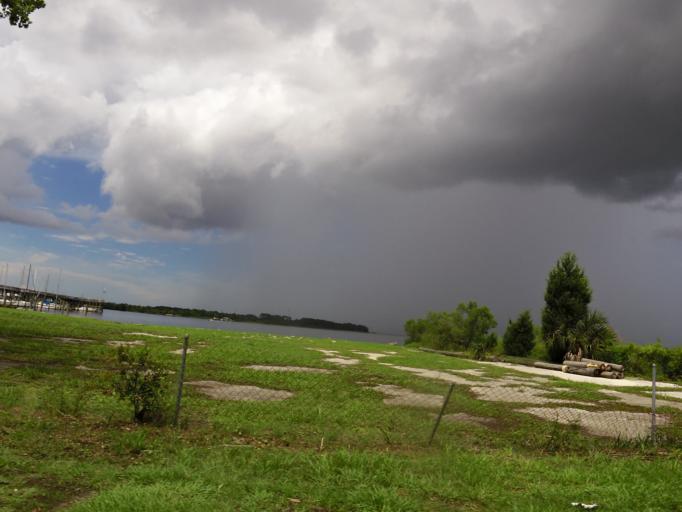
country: US
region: Florida
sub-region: Duval County
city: Jacksonville
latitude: 30.3885
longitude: -81.6411
